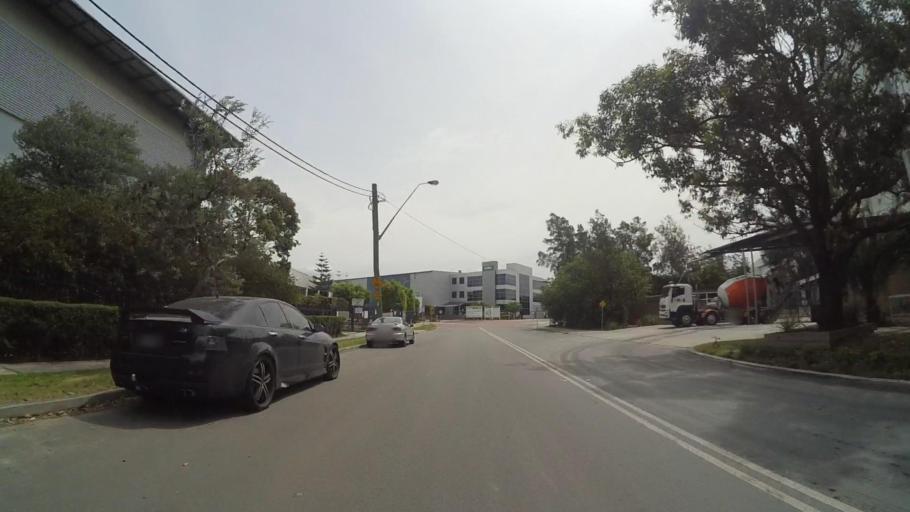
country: AU
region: New South Wales
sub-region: Botany Bay
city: Mascot
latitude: -33.9232
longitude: 151.1790
